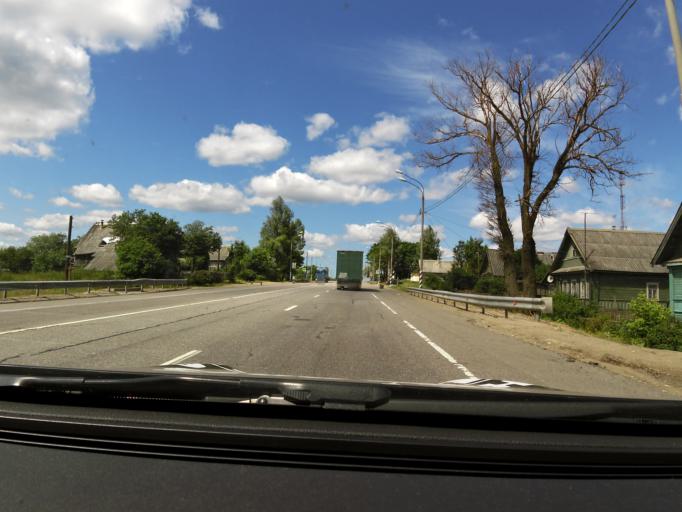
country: RU
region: Tverskaya
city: Kuzhenkino
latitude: 57.7589
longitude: 33.9600
